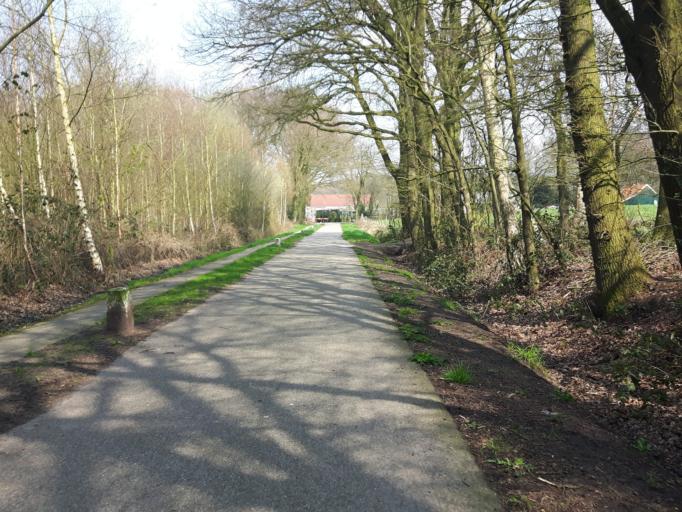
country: NL
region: Overijssel
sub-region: Gemeente Enschede
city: Enschede
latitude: 52.1887
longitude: 6.8467
